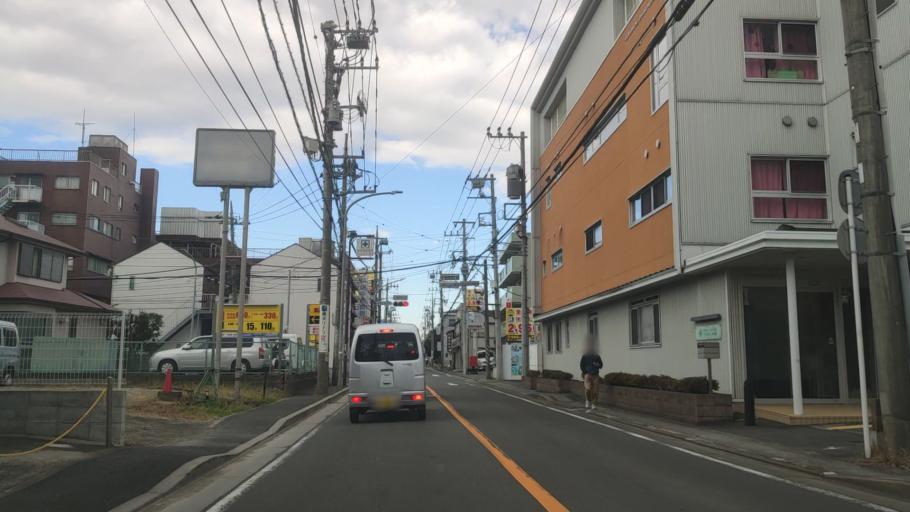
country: JP
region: Kanagawa
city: Fujisawa
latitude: 35.4220
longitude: 139.5335
